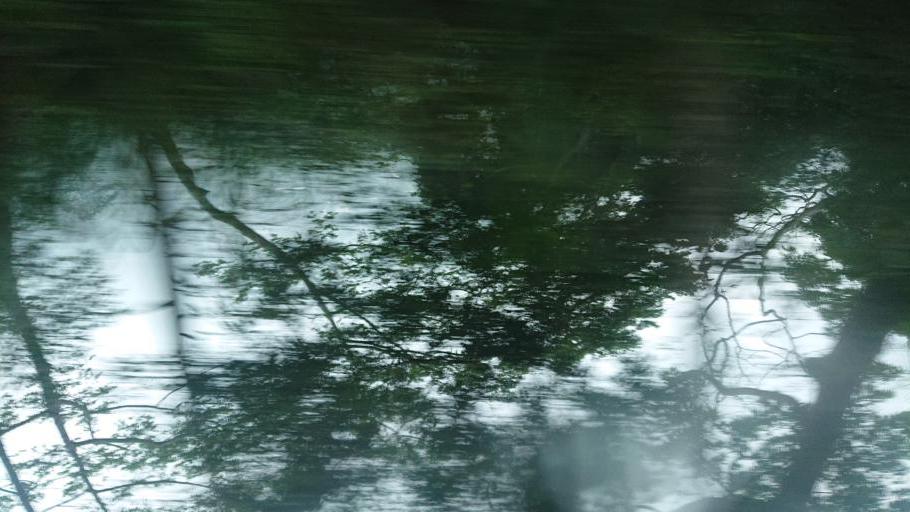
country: TW
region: Taiwan
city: Lugu
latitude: 23.5992
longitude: 120.7137
